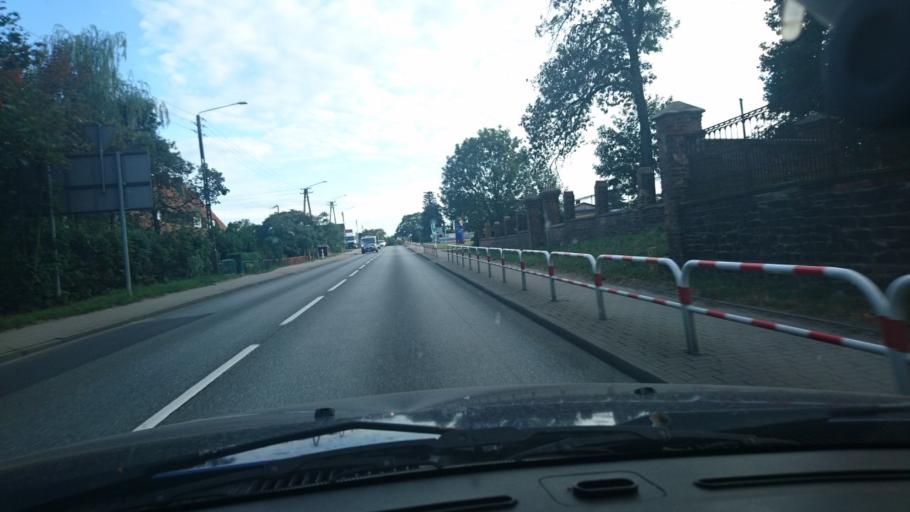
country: PL
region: Opole Voivodeship
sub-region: Powiat kluczborski
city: Byczyna
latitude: 51.1119
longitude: 18.2082
